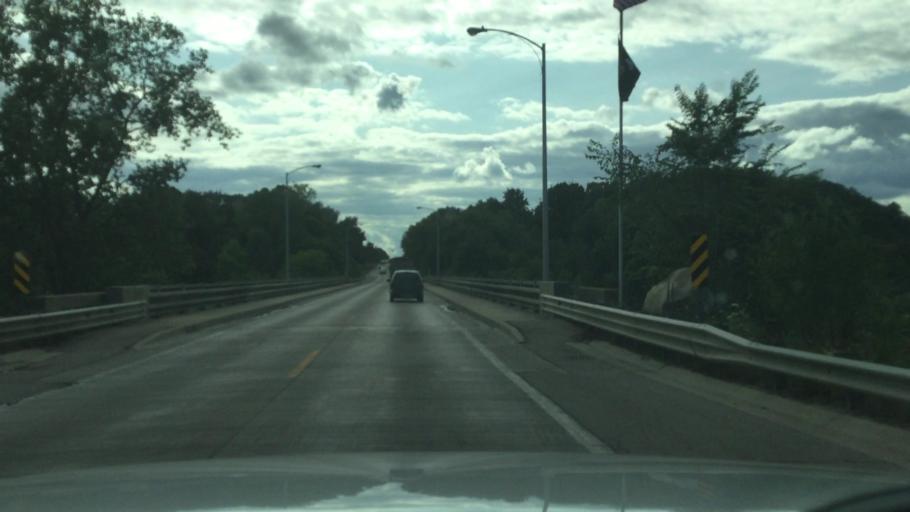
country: US
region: Michigan
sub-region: Ionia County
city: Belding
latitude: 43.0889
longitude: -85.2342
